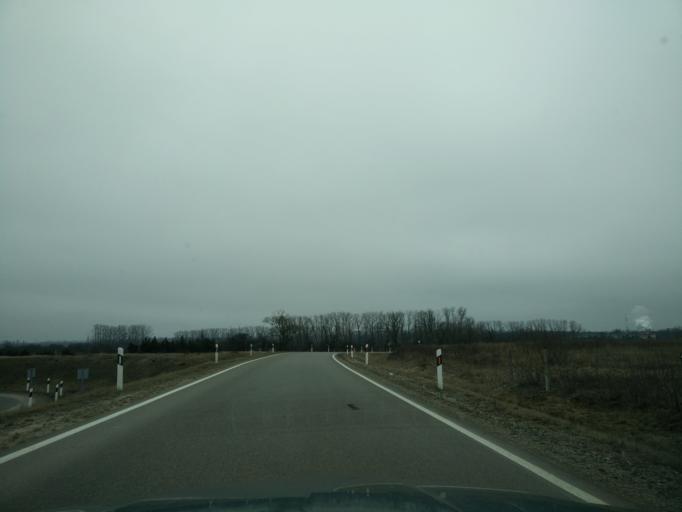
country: LT
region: Klaipedos apskritis
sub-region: Klaipeda
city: Klaipeda
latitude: 55.7316
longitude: 21.1832
